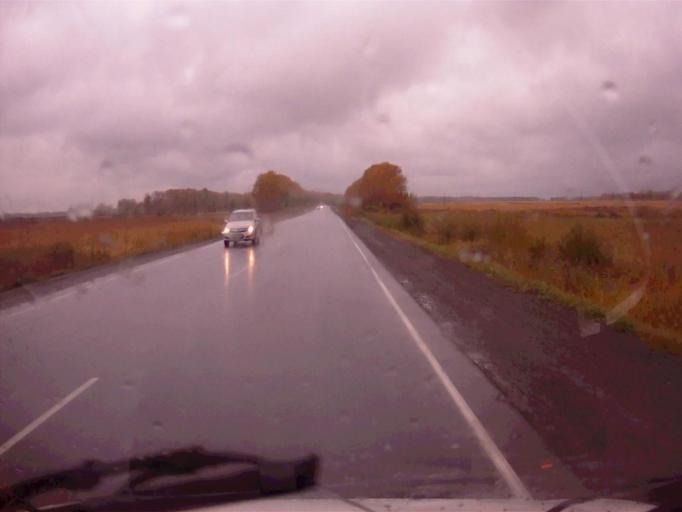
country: RU
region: Chelyabinsk
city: Argayash
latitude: 55.4466
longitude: 60.9482
